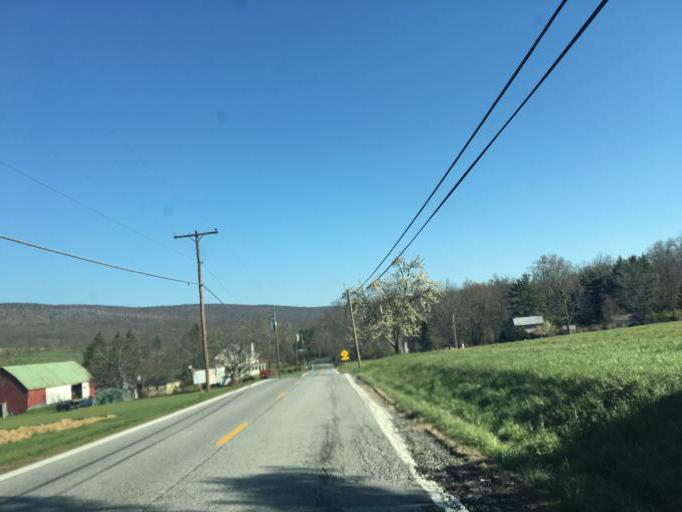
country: US
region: Maryland
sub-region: Washington County
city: Cavetown
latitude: 39.5892
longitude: -77.5581
